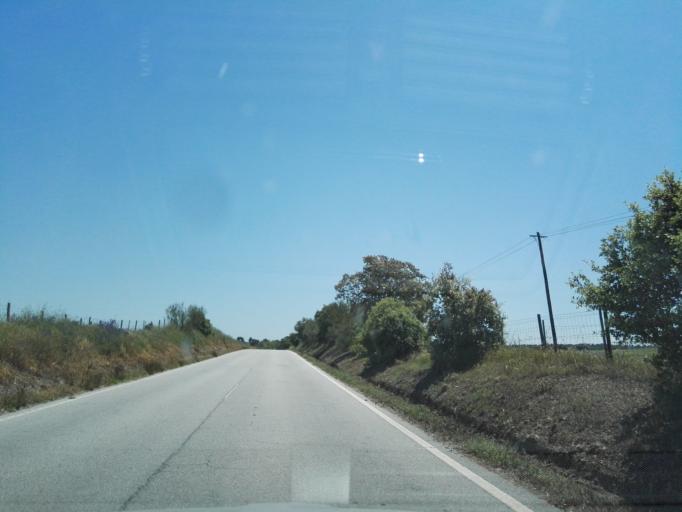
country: PT
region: Portalegre
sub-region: Arronches
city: Arronches
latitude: 39.0087
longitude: -7.2383
